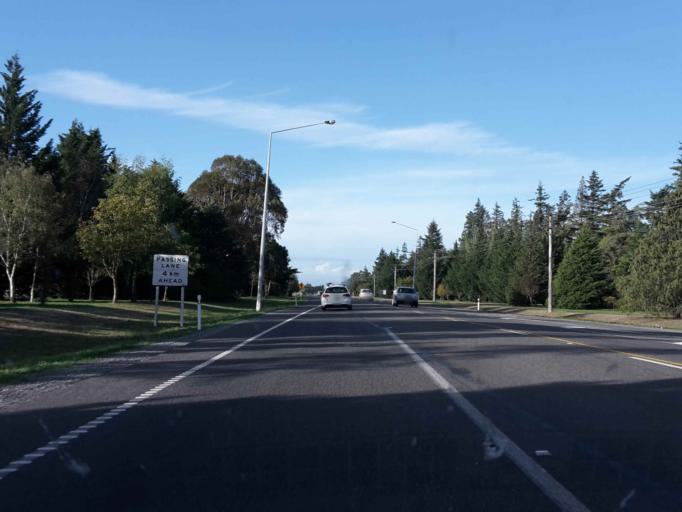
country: NZ
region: Canterbury
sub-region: Ashburton District
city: Ashburton
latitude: -43.8807
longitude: 171.7825
